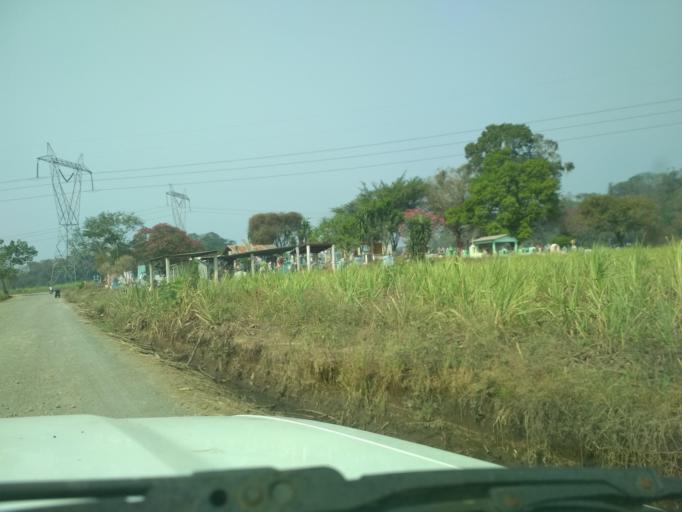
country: MX
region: Oaxaca
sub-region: Cosolapa
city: Cosolapa
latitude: 18.6097
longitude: -96.6305
